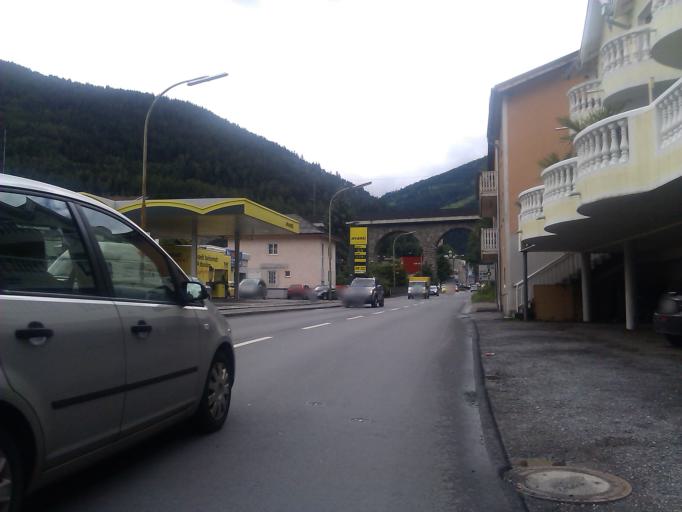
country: AT
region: Tyrol
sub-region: Politischer Bezirk Landeck
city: Landeck
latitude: 47.1419
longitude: 10.5630
